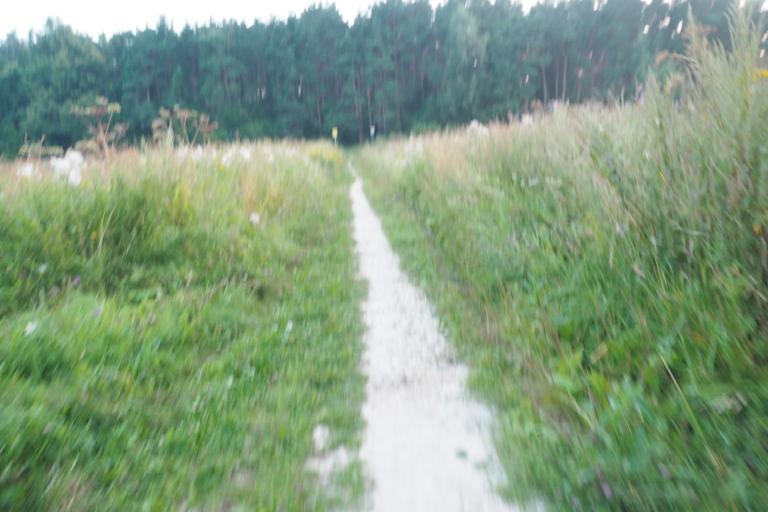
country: RU
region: Moscow
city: Orekhovo-Borisovo Severnoye
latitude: 55.6018
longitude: 37.6993
